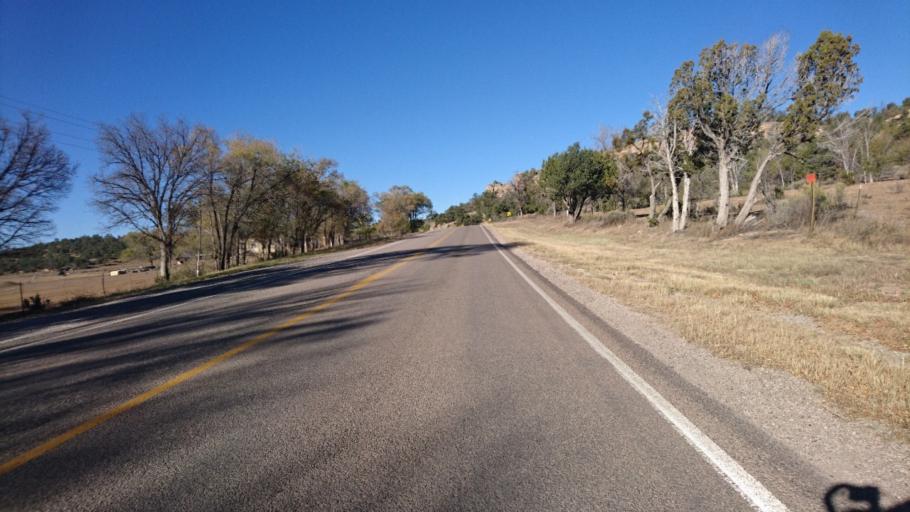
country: US
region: New Mexico
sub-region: McKinley County
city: Black Rock
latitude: 35.1333
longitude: -108.5136
